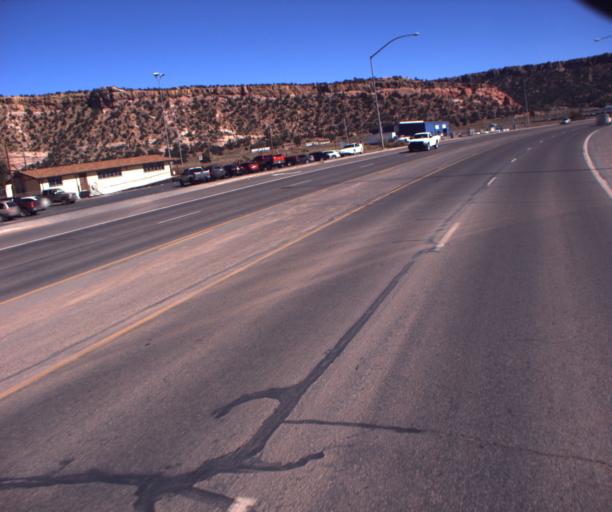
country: US
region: Arizona
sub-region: Apache County
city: Window Rock
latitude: 35.6628
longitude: -109.0479
